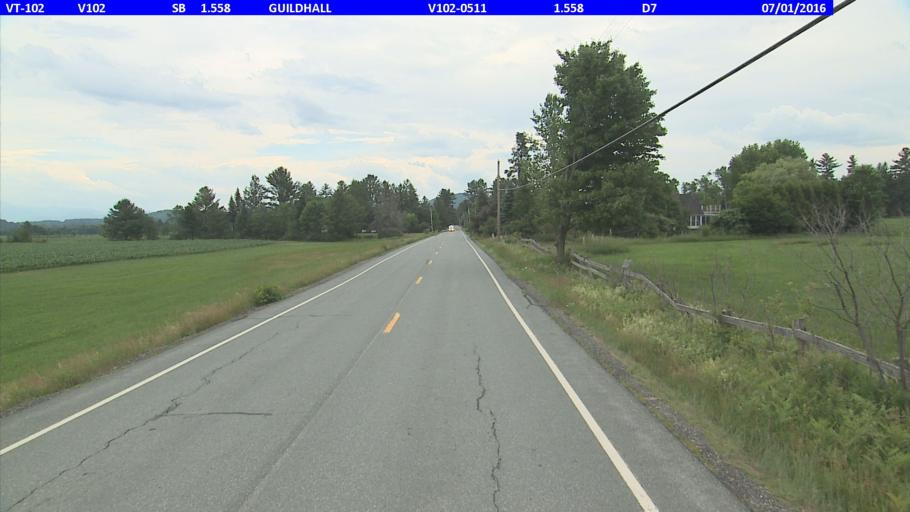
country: US
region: New Hampshire
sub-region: Coos County
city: Lancaster
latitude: 44.5178
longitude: -71.5947
